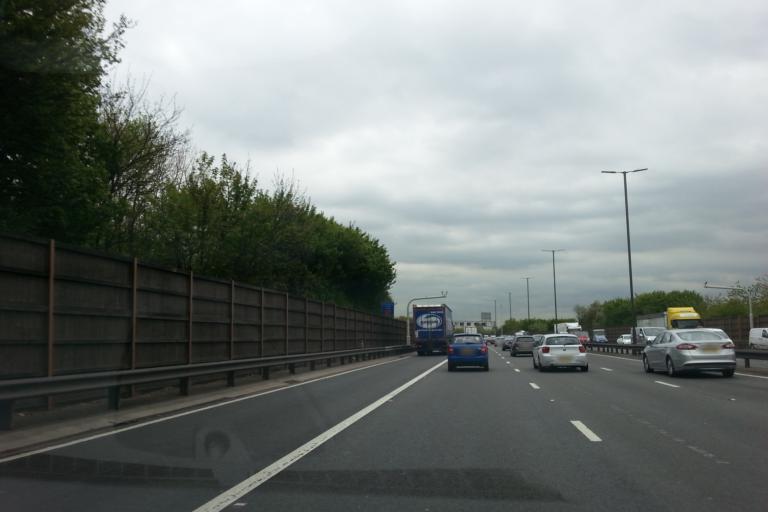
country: GB
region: England
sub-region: City and Borough of Birmingham
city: Hockley
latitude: 52.5419
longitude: -1.9131
